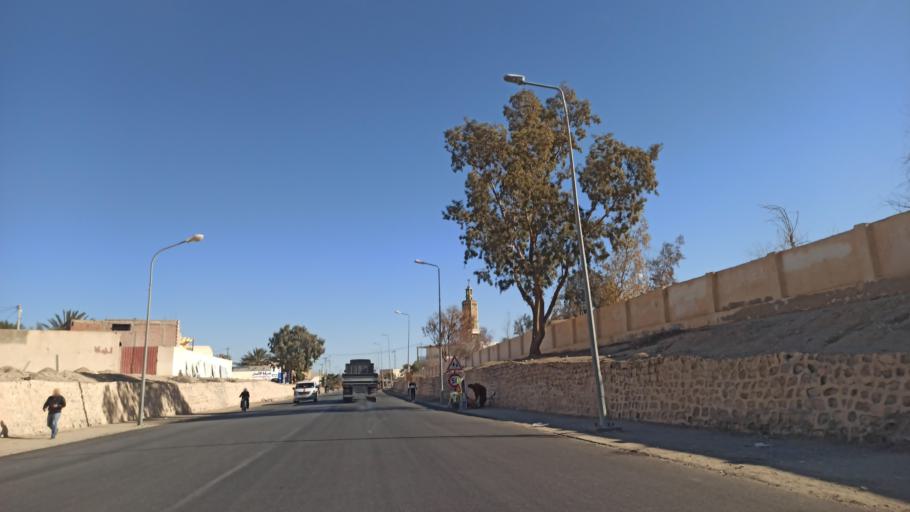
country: TN
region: Gafsa
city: Al Metlaoui
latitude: 34.3148
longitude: 8.3929
